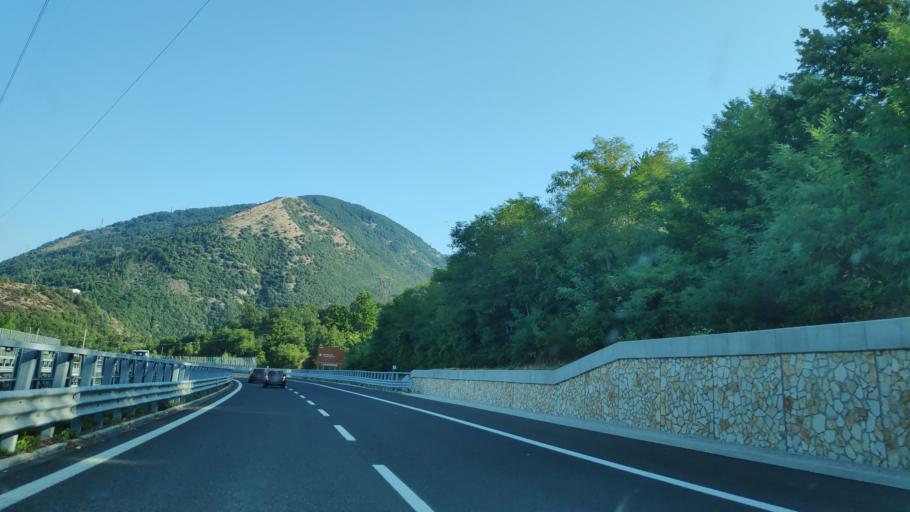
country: IT
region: Basilicate
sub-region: Provincia di Potenza
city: Lagonegro
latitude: 40.1202
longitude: 15.7842
